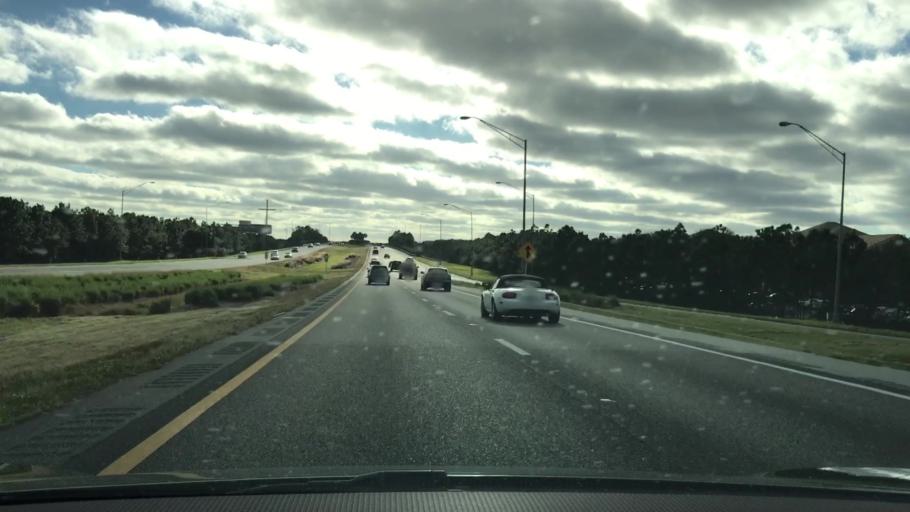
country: US
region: Florida
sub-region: Orange County
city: Hunters Creek
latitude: 28.3707
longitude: -81.4286
